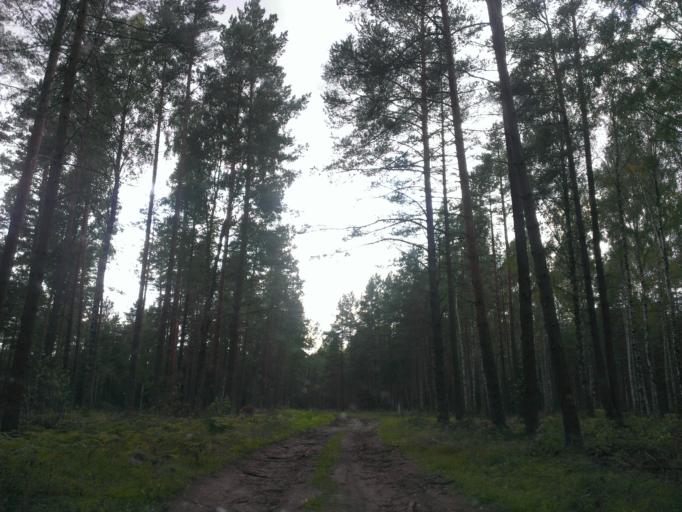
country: LV
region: Incukalns
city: Vangazi
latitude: 57.1086
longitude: 24.5362
